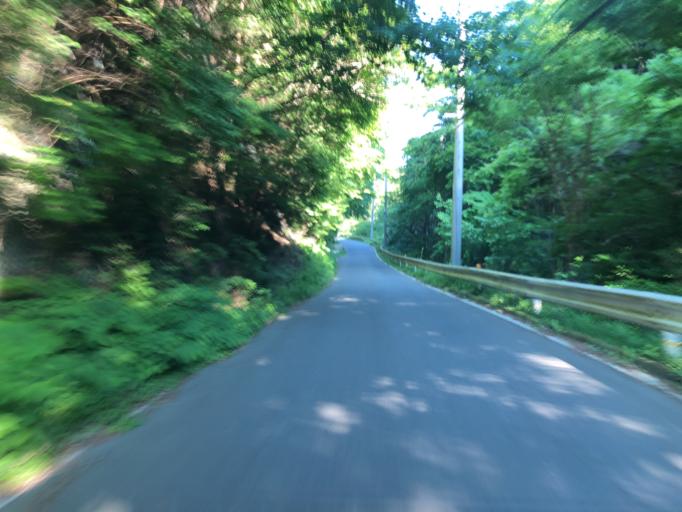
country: JP
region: Ibaraki
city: Kitaibaraki
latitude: 36.8683
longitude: 140.6583
